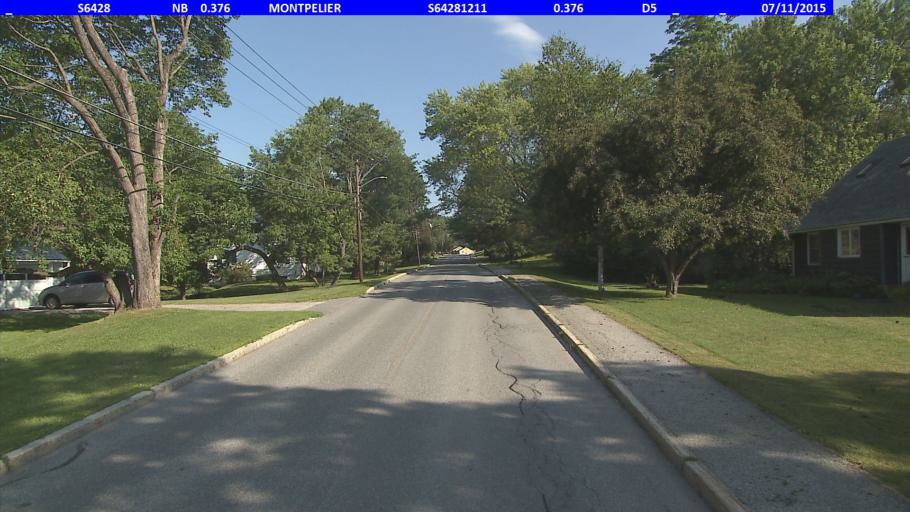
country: US
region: Vermont
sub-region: Washington County
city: Montpelier
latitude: 44.2682
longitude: -72.5879
